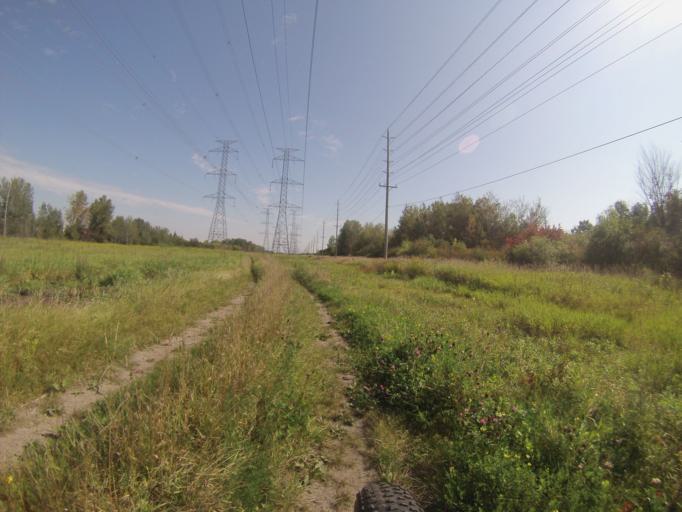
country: CA
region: Ontario
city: Ottawa
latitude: 45.3742
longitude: -75.6380
